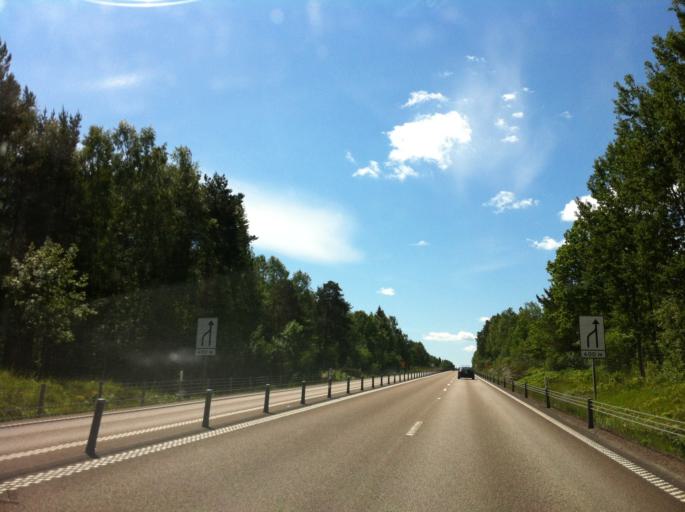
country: SE
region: Vaestra Goetaland
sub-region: Melleruds Kommun
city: Mellerud
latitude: 58.7925
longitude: 12.5180
